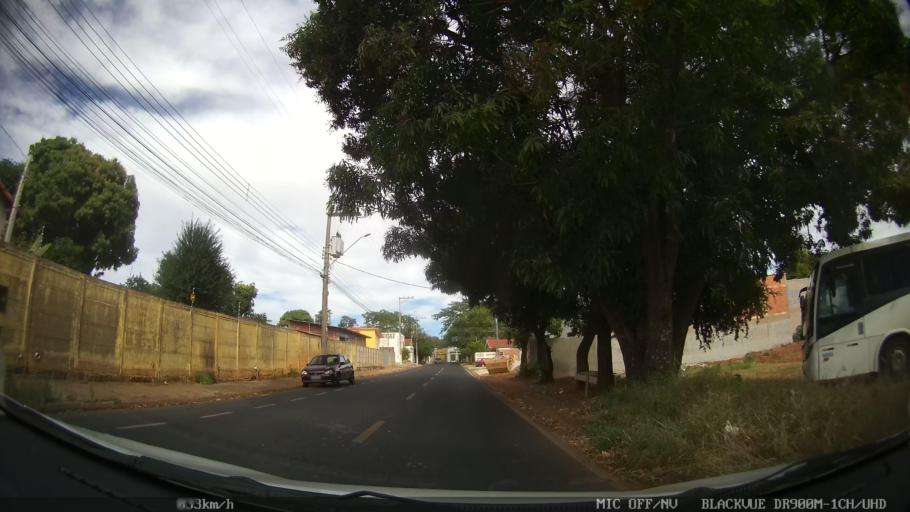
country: BR
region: Sao Paulo
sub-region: Catanduva
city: Catanduva
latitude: -21.1503
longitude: -48.9632
